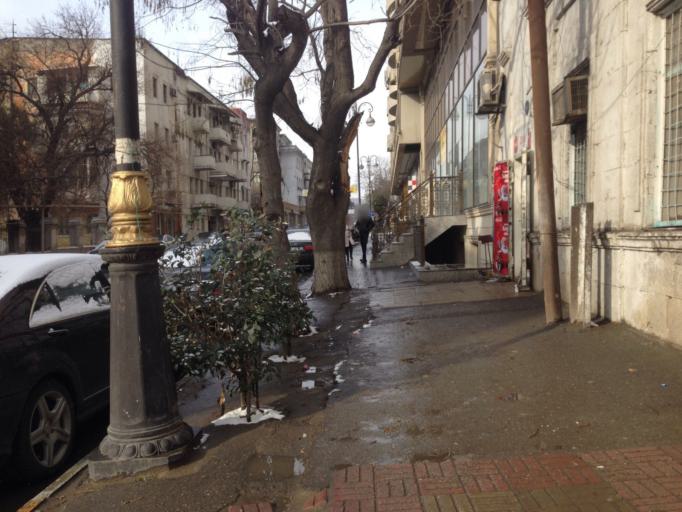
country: AZ
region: Baki
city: Baku
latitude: 40.3909
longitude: 49.8588
